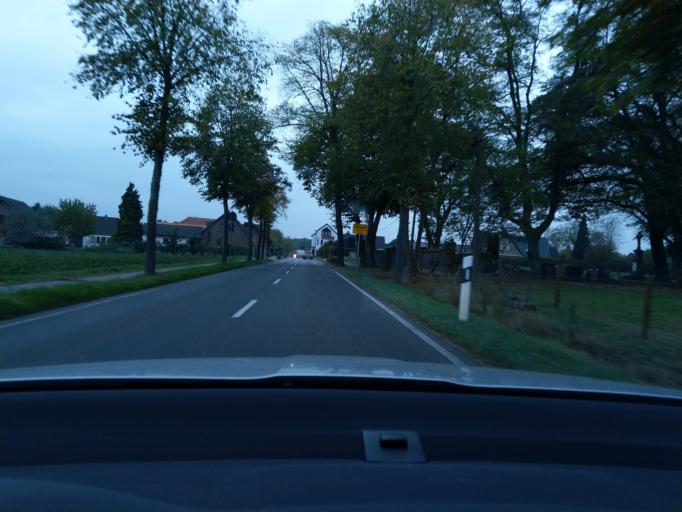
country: DE
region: North Rhine-Westphalia
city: Wegberg
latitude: 51.1712
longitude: 6.2866
